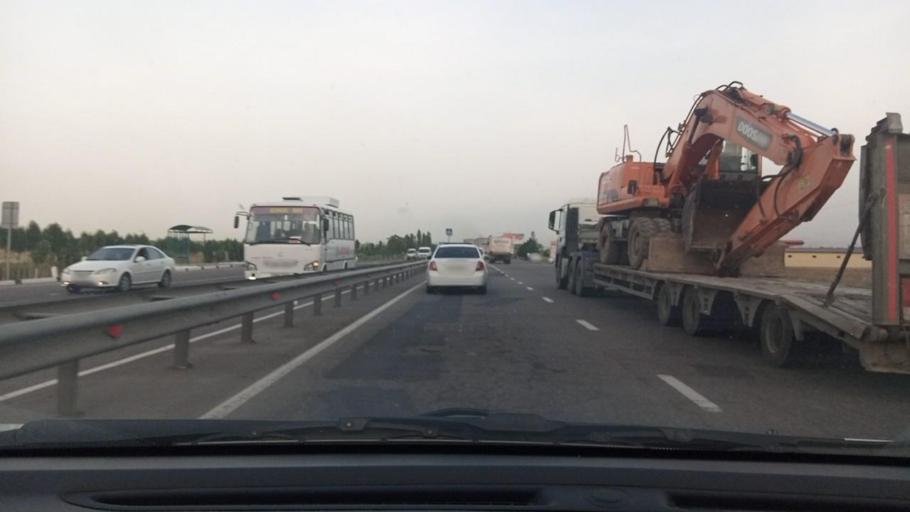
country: UZ
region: Toshkent
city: Ohangaron
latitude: 40.9197
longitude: 69.5986
